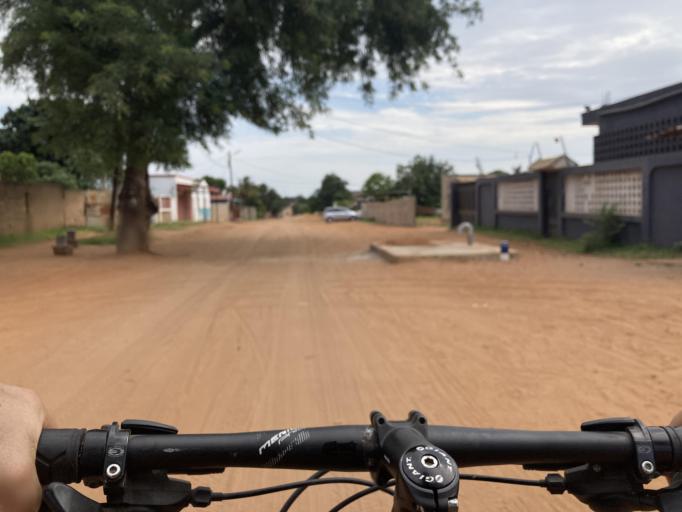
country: MZ
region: Maputo City
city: Maputo
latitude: -25.8888
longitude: 32.6091
